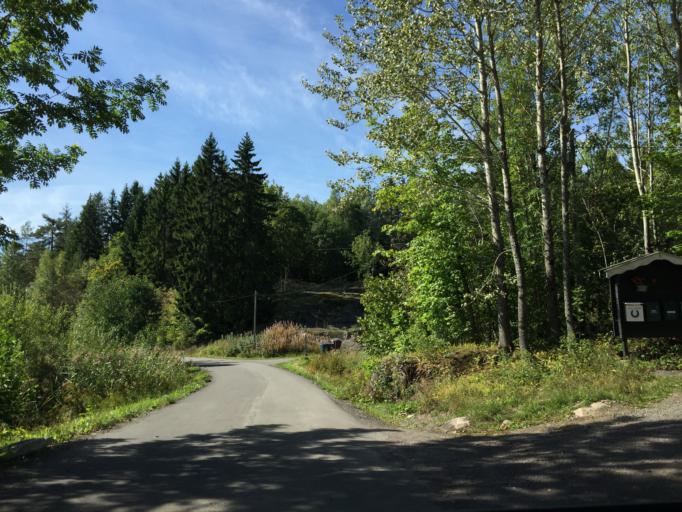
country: NO
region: Vestfold
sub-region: Hof
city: Hof
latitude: 59.4748
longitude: 10.1441
